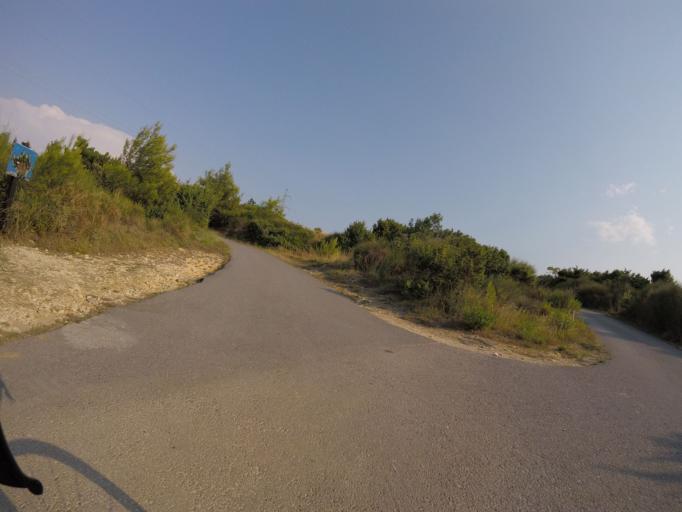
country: HR
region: Primorsko-Goranska
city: Lopar
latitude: 44.8403
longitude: 14.7297
